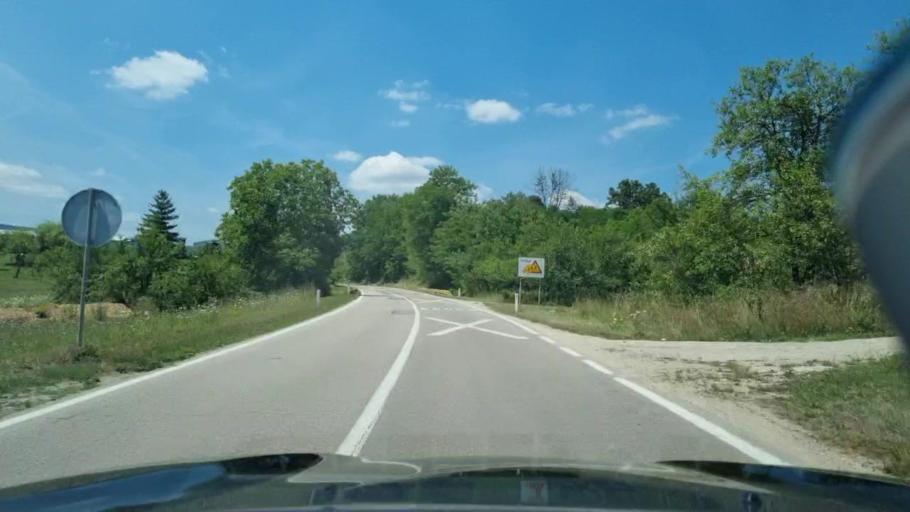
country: BA
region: Federation of Bosnia and Herzegovina
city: Velagici
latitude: 44.5605
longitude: 16.7238
